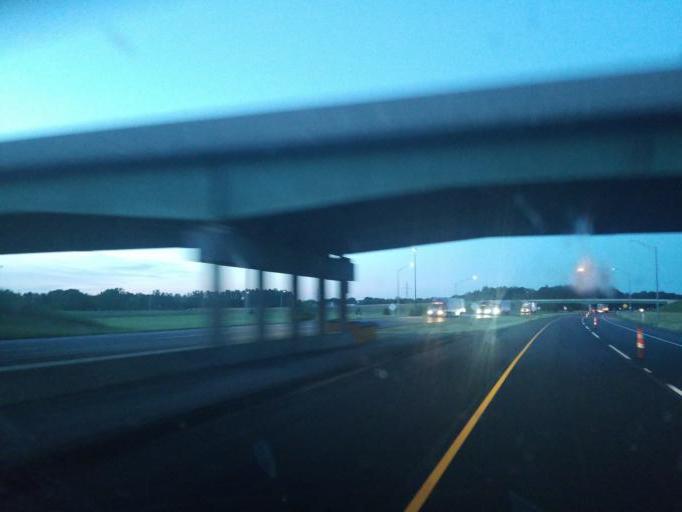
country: US
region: Indiana
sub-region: Saint Joseph County
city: Granger
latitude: 41.7302
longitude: -86.1446
